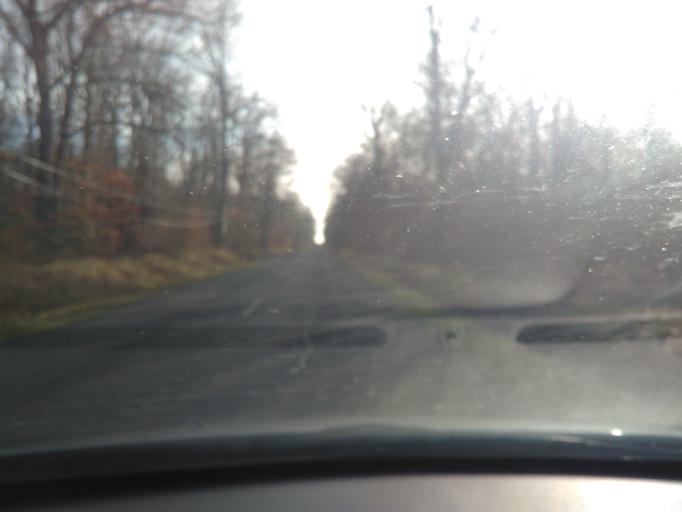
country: FR
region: Bourgogne
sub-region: Departement de la Nievre
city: Saint-Parize-le-Chatel
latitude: 46.7968
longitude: 3.2708
